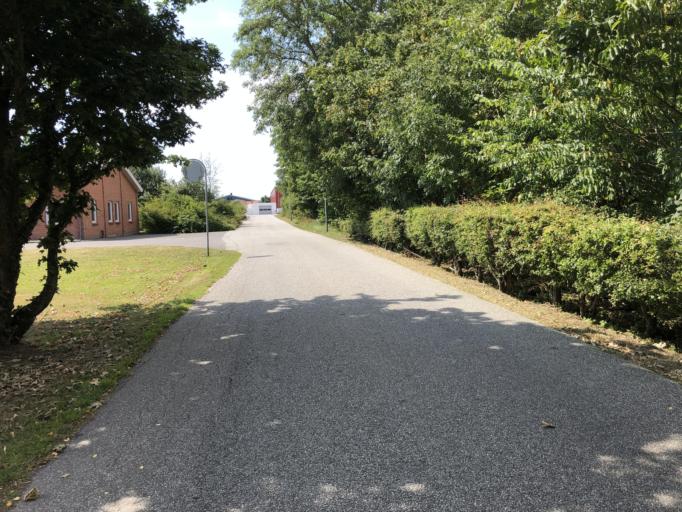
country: DK
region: Central Jutland
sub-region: Lemvig Kommune
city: Lemvig
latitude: 56.5460
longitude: 8.2991
